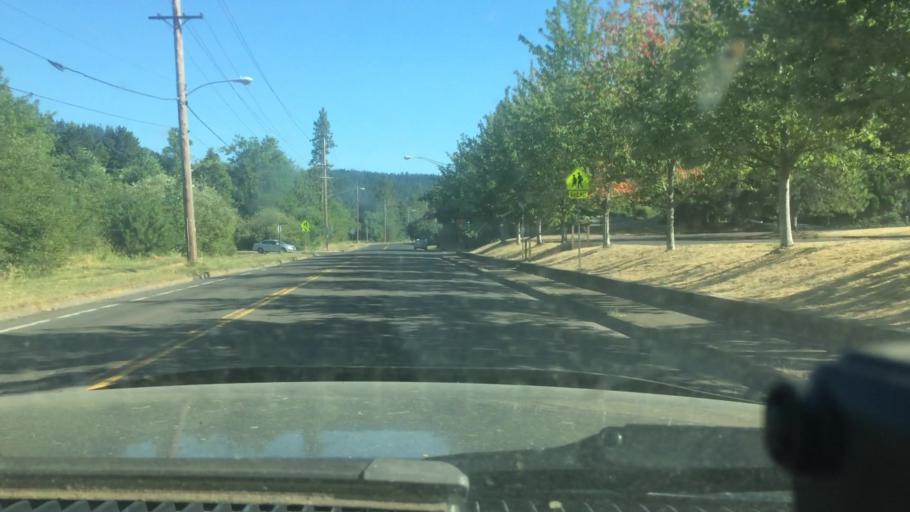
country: US
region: Oregon
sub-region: Lane County
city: Eugene
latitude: 44.0111
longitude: -123.0769
